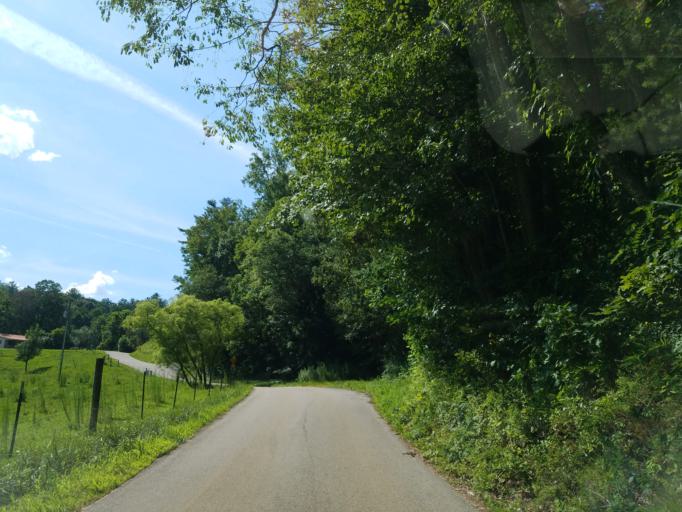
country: US
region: Georgia
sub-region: Dawson County
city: Dawsonville
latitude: 34.5688
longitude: -84.1510
